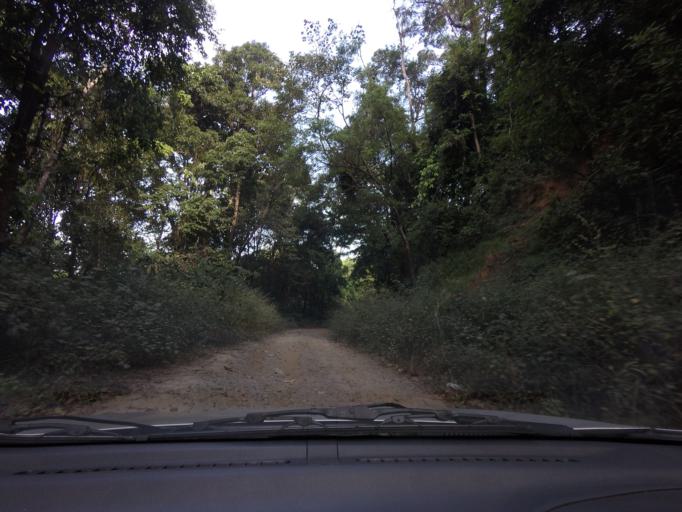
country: IN
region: Karnataka
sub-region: Kodagu
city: Somvarpet
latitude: 12.7136
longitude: 75.6698
